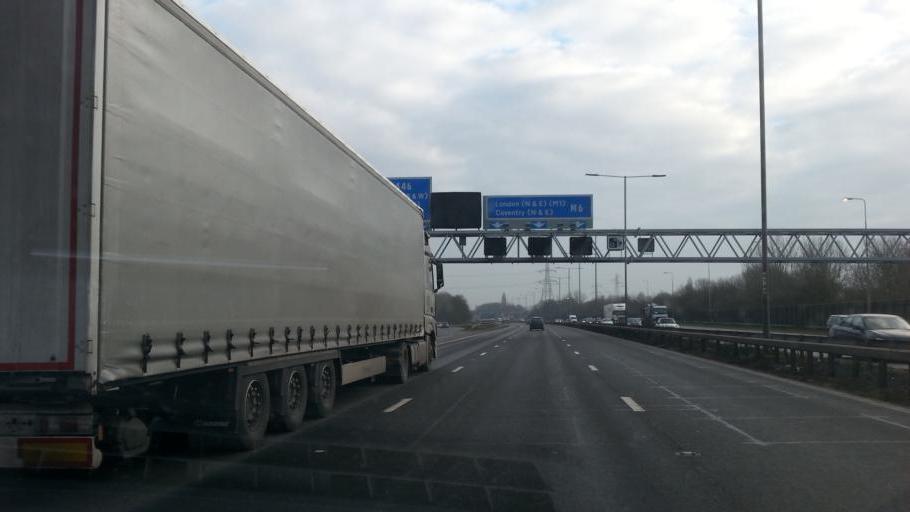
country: GB
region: England
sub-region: Solihull
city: Chelmsley Wood
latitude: 52.4840
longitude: -1.7241
